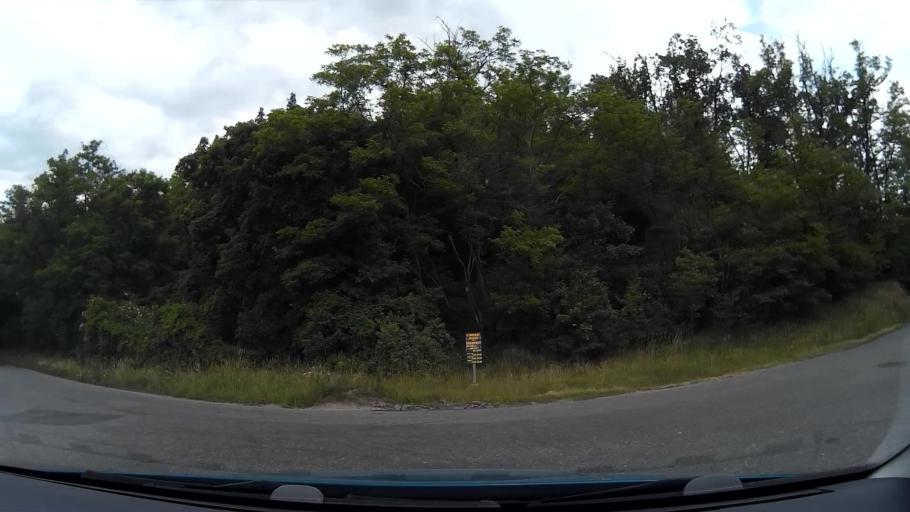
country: CZ
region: South Moravian
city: Ostopovice
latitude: 49.1456
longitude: 16.5311
